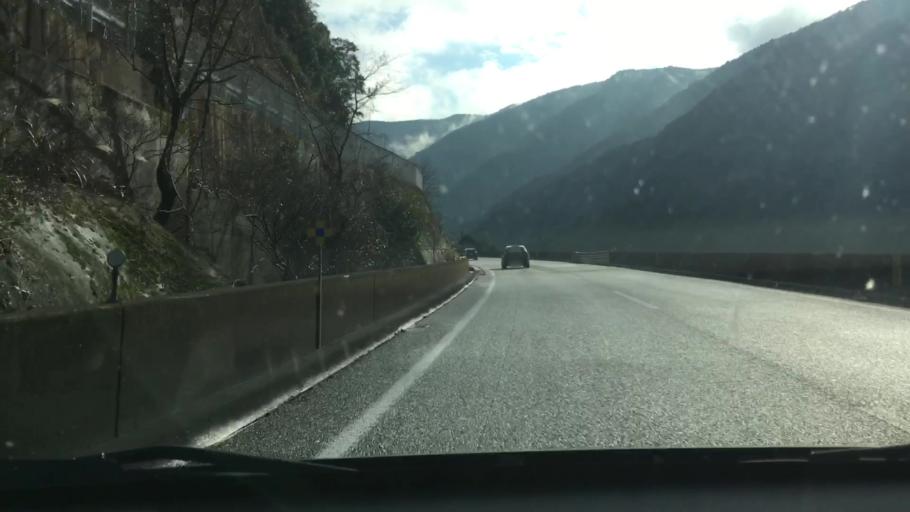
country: JP
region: Kumamoto
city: Yatsushiro
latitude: 32.4142
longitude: 130.6956
